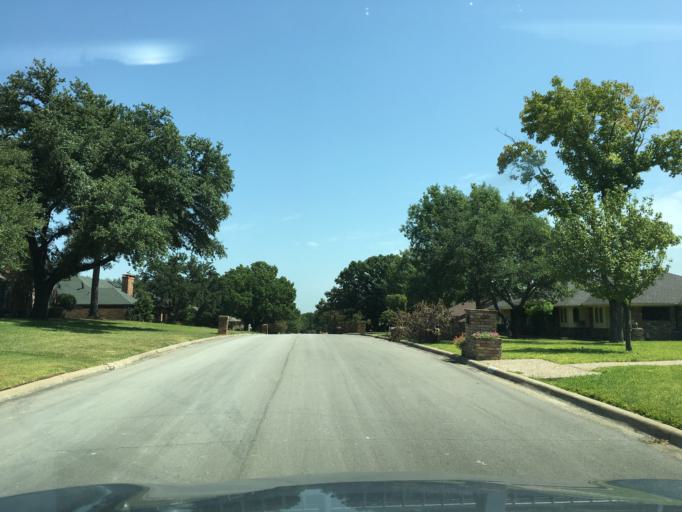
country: US
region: Texas
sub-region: Dallas County
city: Rowlett
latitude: 32.8731
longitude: -96.6016
